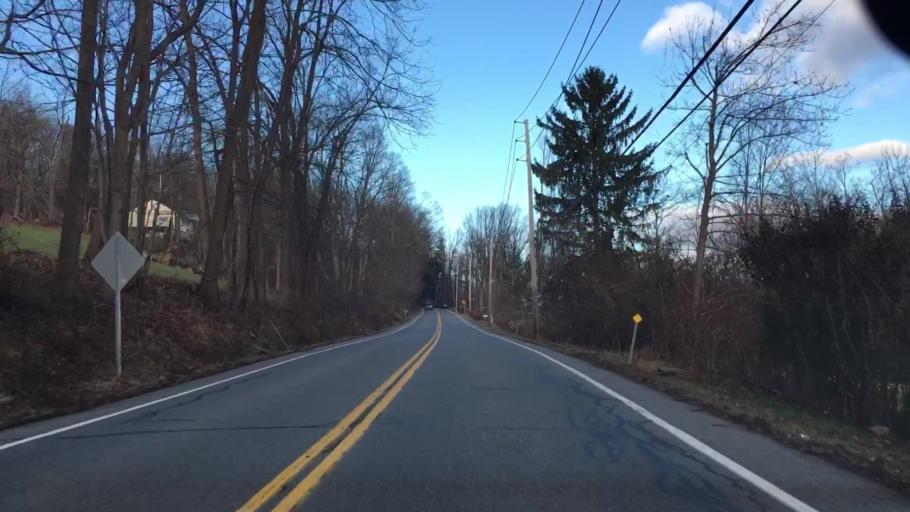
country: US
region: New York
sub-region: Putnam County
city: Lake Carmel
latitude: 41.4595
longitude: -73.6499
